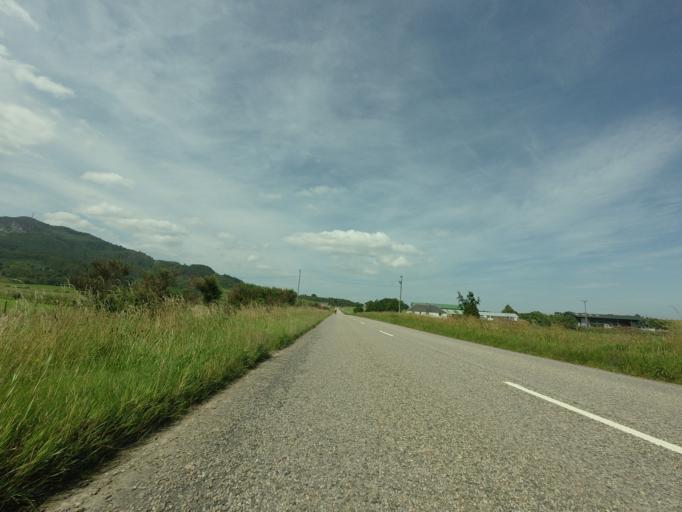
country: GB
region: Scotland
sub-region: Highland
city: Tain
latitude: 57.8454
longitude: -4.1989
